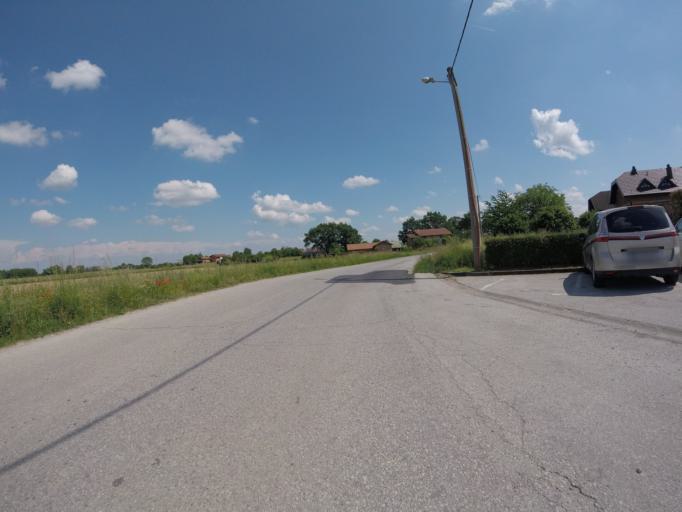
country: HR
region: Zagrebacka
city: Gradici
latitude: 45.6786
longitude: 16.0624
